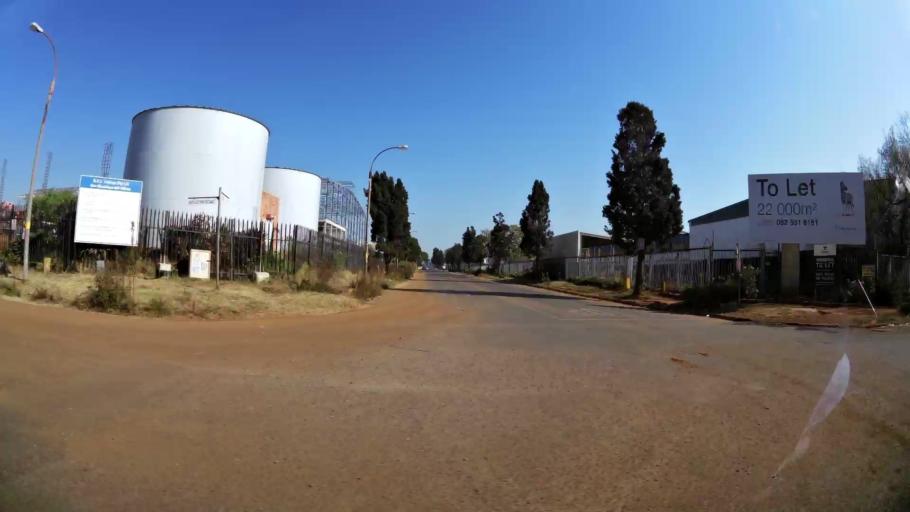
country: ZA
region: Gauteng
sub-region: City of Johannesburg Metropolitan Municipality
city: Modderfontein
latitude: -26.1410
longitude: 28.2145
